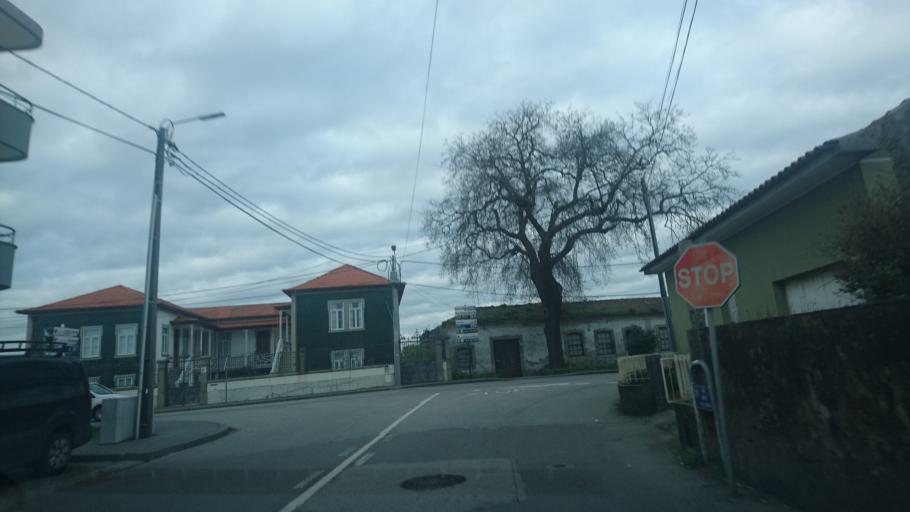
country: PT
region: Aveiro
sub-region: Santa Maria da Feira
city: Rio Meao
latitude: 40.9589
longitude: -8.5928
